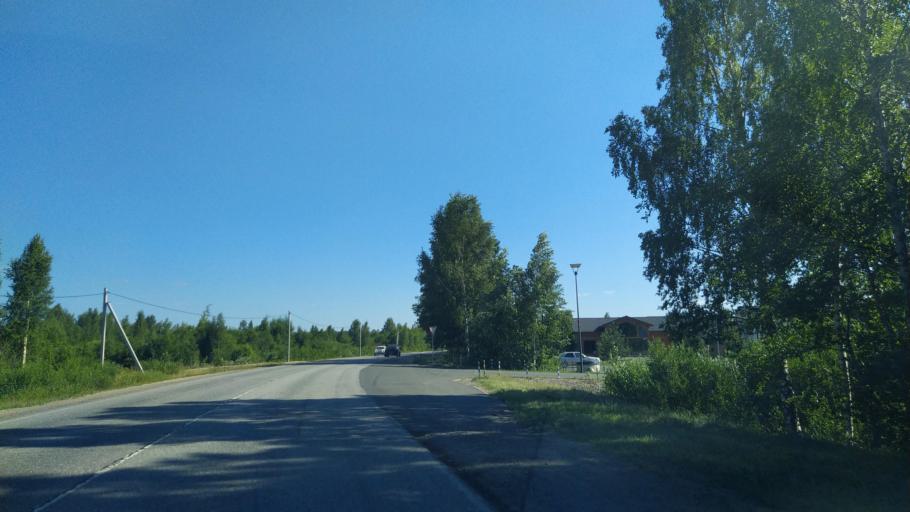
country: RU
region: Leningrad
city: Imeni Morozova
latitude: 59.9987
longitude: 31.0507
